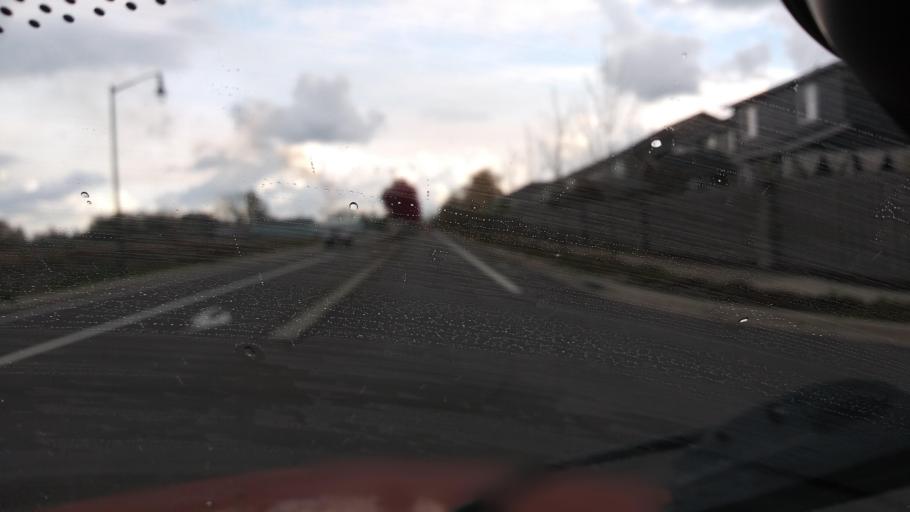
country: US
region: Oregon
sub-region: Washington County
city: Forest Grove
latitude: 45.5391
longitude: -123.1115
